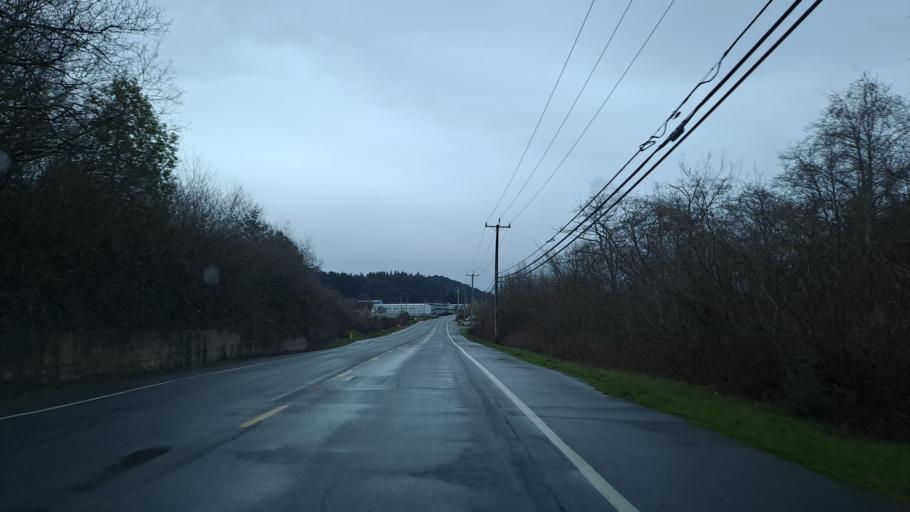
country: US
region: California
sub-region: Humboldt County
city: Fortuna
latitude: 40.5878
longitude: -124.1328
